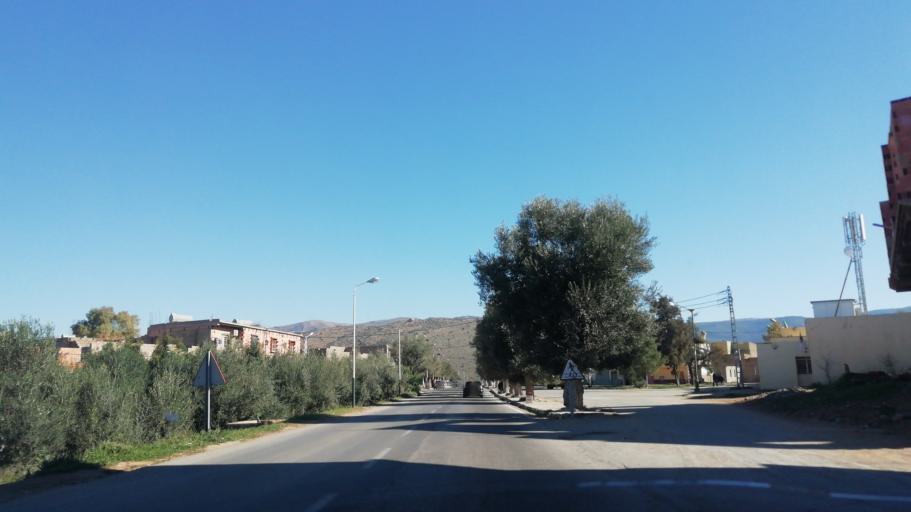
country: DZ
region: Tlemcen
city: Beni Mester
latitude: 34.8426
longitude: -1.4751
